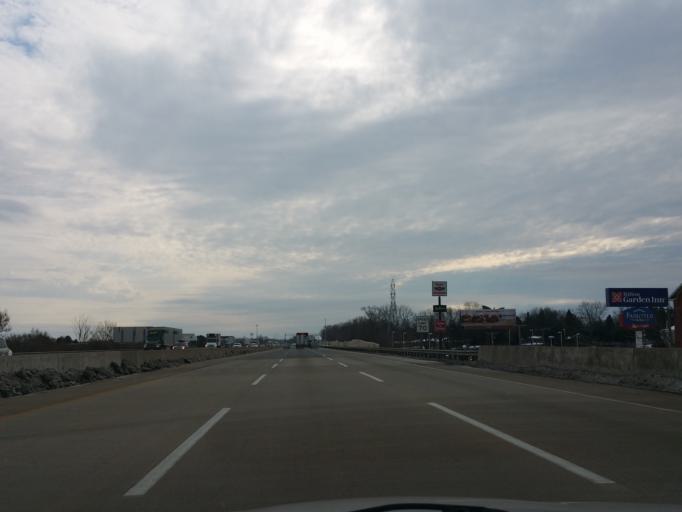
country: US
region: Illinois
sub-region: Winnebago County
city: Cherry Valley
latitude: 42.2711
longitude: -88.9650
